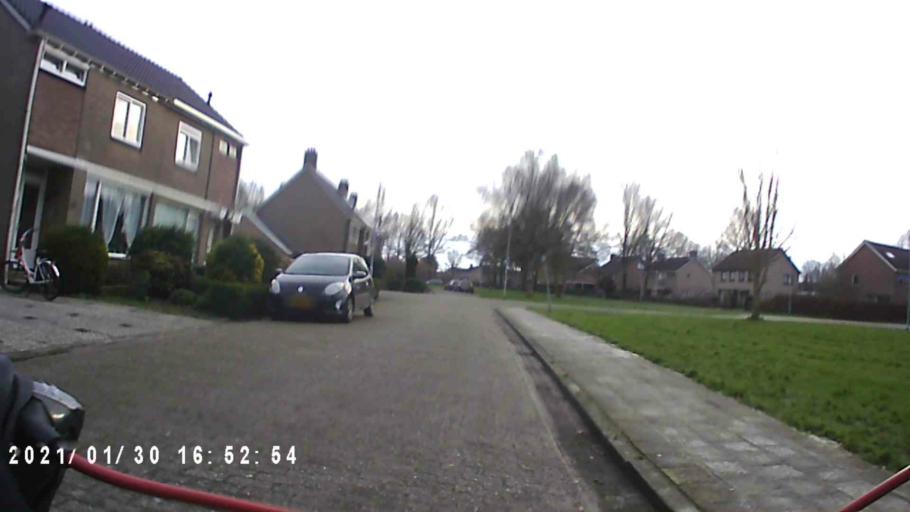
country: NL
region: Groningen
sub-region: Gemeente Leek
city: Leek
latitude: 53.1604
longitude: 6.3801
